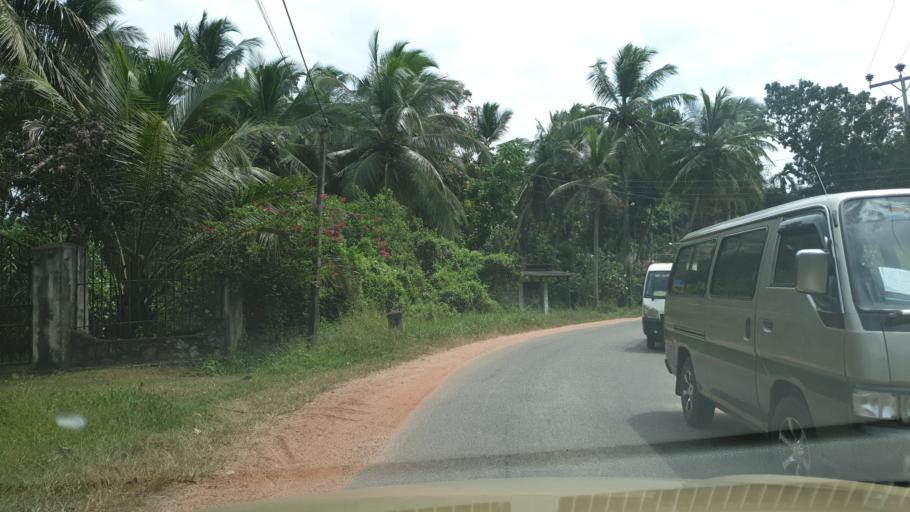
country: LK
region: North Western
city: Kuliyapitiya
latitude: 7.3464
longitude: 79.9859
